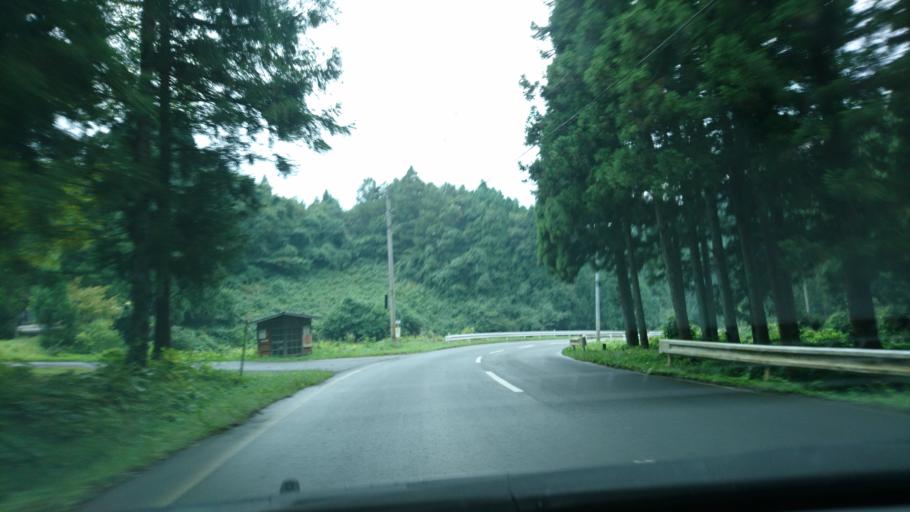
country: JP
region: Iwate
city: Mizusawa
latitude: 39.0354
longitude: 141.1945
